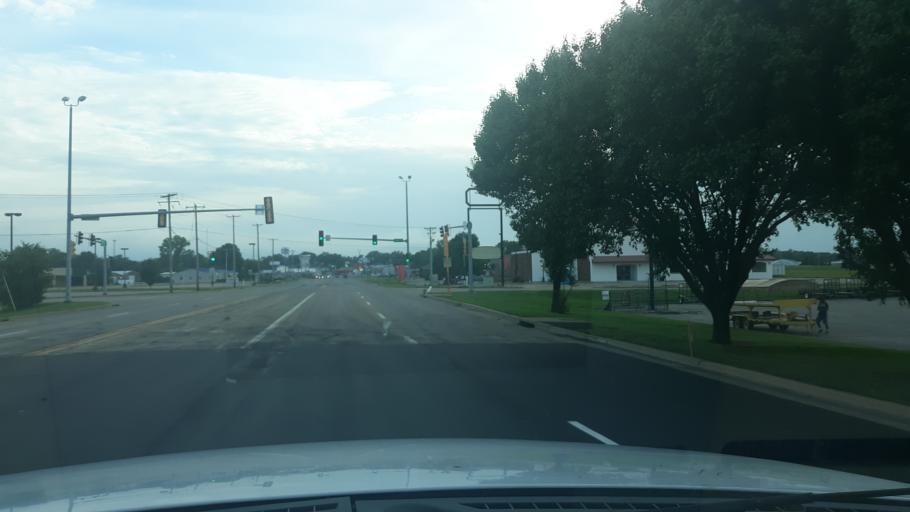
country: US
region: Illinois
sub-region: Saline County
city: Harrisburg
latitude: 37.7432
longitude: -88.5260
